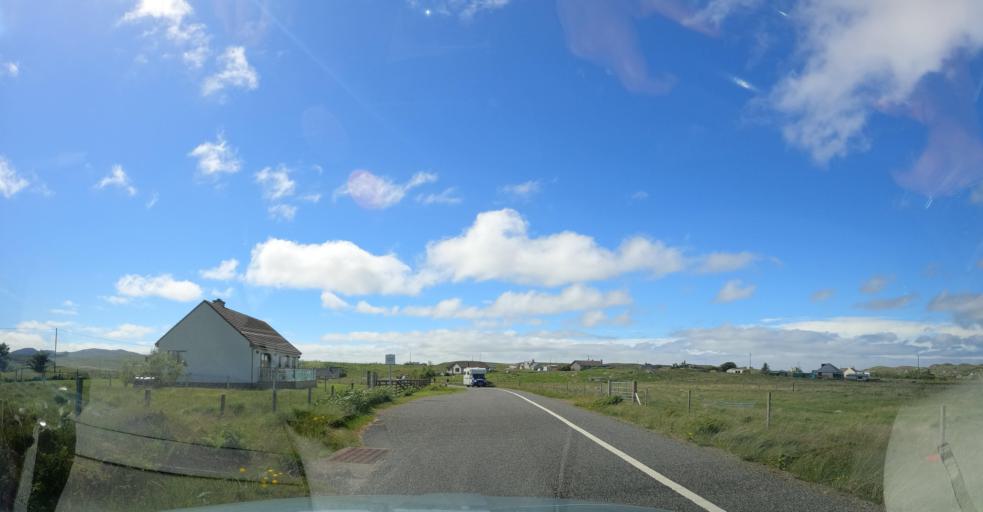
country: GB
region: Scotland
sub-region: Eilean Siar
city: Harris
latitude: 58.1987
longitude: -6.7324
